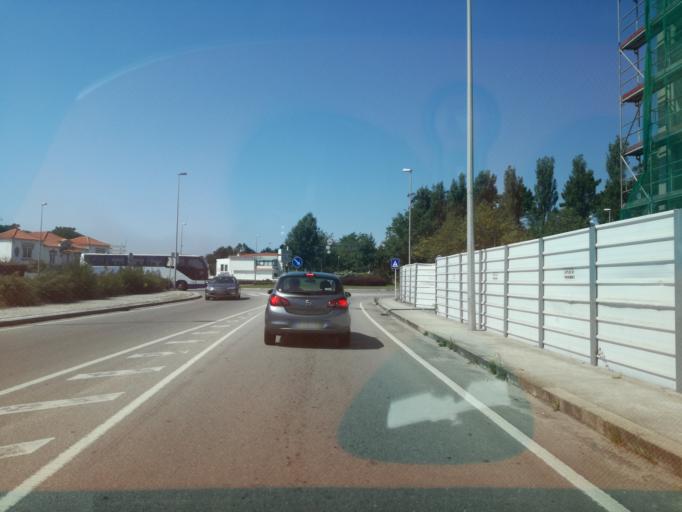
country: PT
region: Braga
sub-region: Esposende
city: Esposende
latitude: 41.5391
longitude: -8.7813
